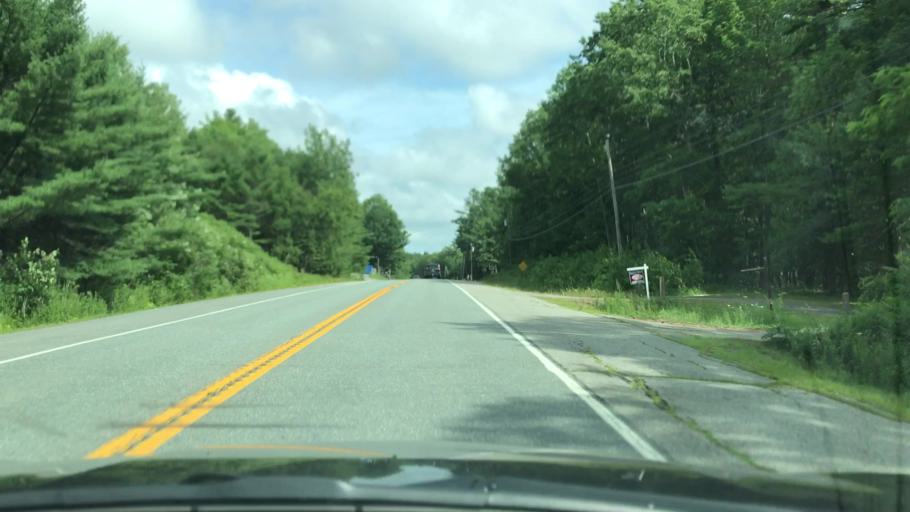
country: US
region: Maine
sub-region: Hancock County
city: Orland
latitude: 44.5663
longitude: -68.6708
